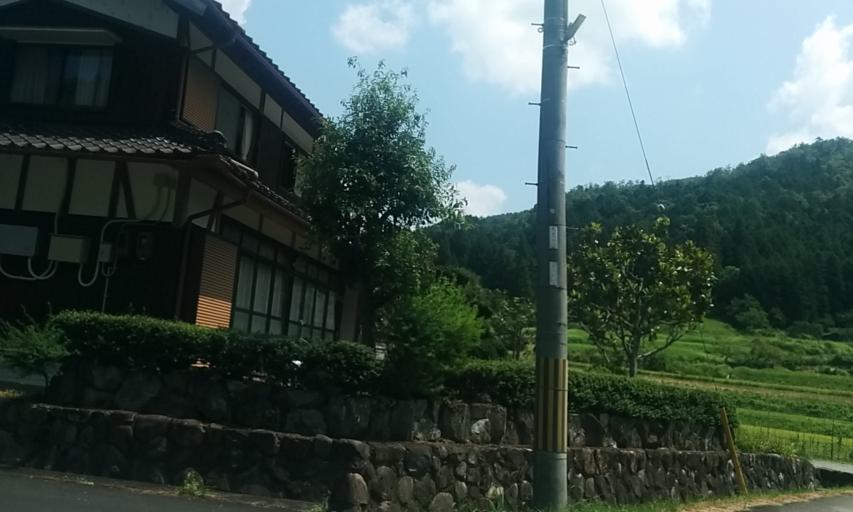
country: JP
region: Kyoto
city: Ayabe
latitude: 35.2109
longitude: 135.2019
